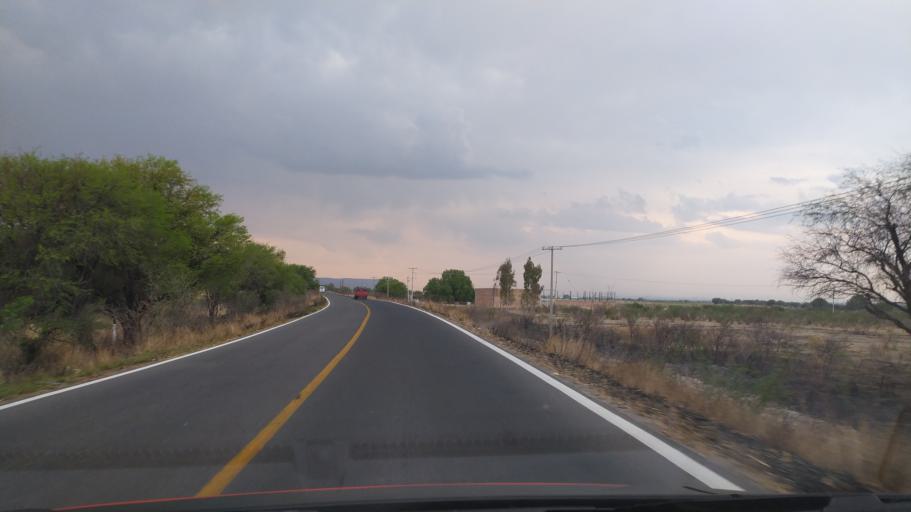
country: MX
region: Guanajuato
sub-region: San Francisco del Rincon
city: San Ignacio de Hidalgo
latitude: 20.8216
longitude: -101.9022
